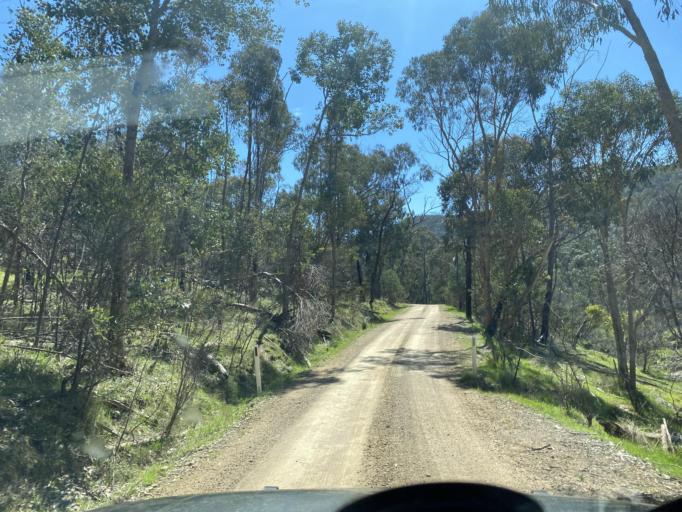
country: AU
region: Victoria
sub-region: Benalla
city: Benalla
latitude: -36.7049
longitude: 146.1778
